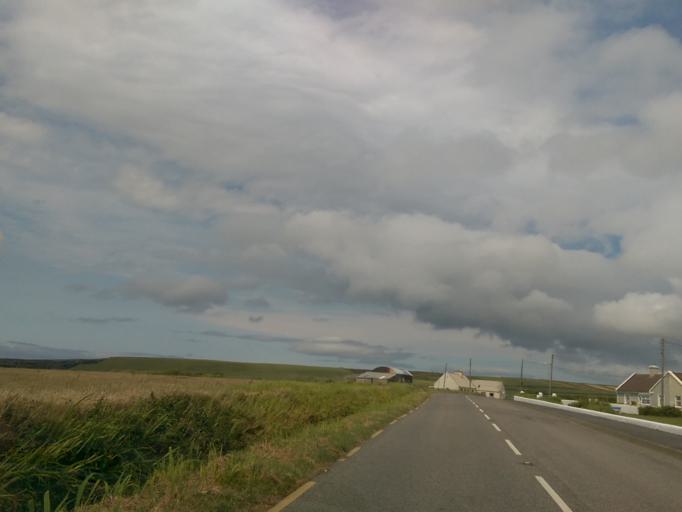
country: IE
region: Munster
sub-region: An Clar
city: Kilrush
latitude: 52.6867
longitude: -9.6413
